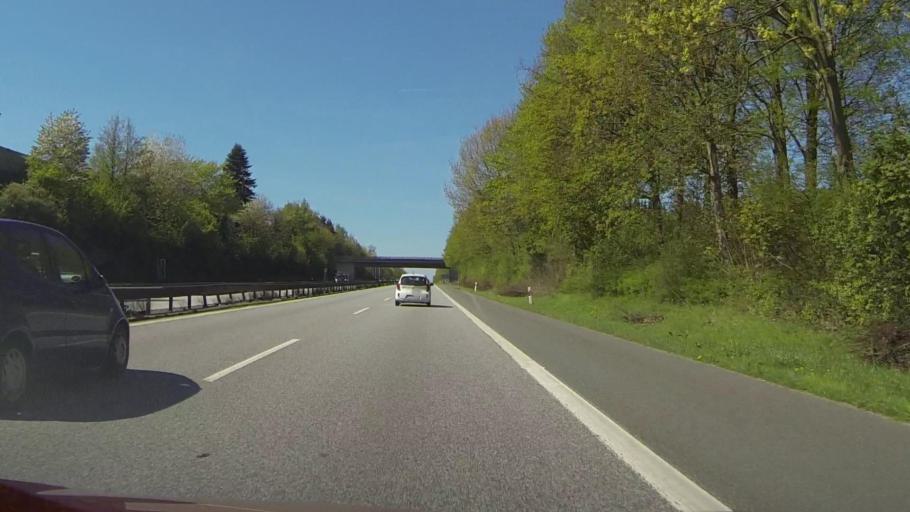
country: DE
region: Schleswig-Holstein
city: Kummerfeld
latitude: 53.6805
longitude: 9.7953
